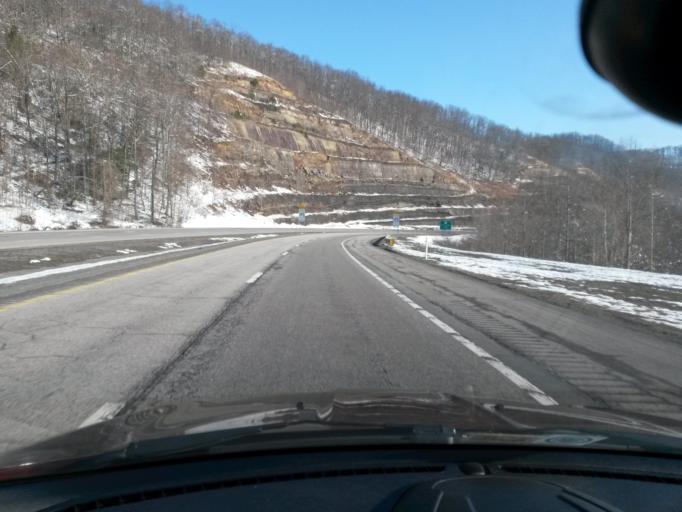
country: US
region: West Virginia
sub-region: Nicholas County
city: Craigsville
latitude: 38.4717
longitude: -80.7789
